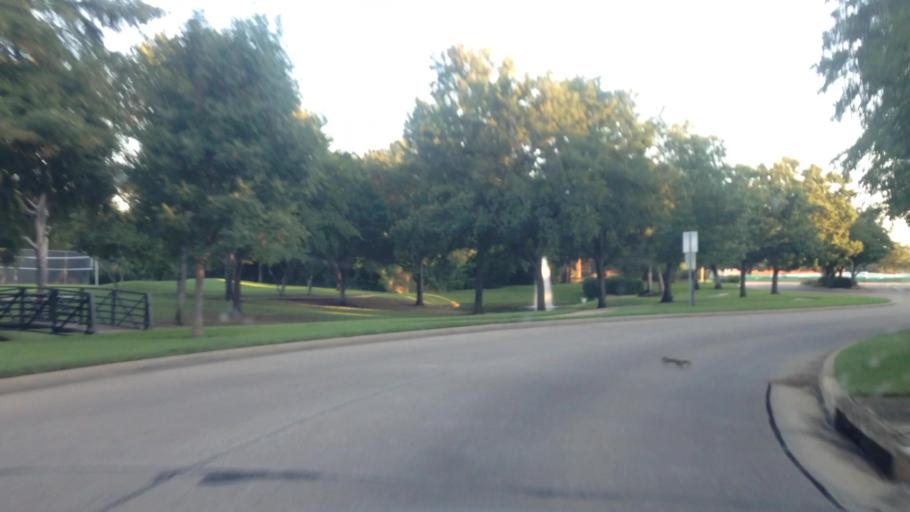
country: US
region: Texas
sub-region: Tarrant County
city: Southlake
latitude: 32.9398
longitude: -97.1628
